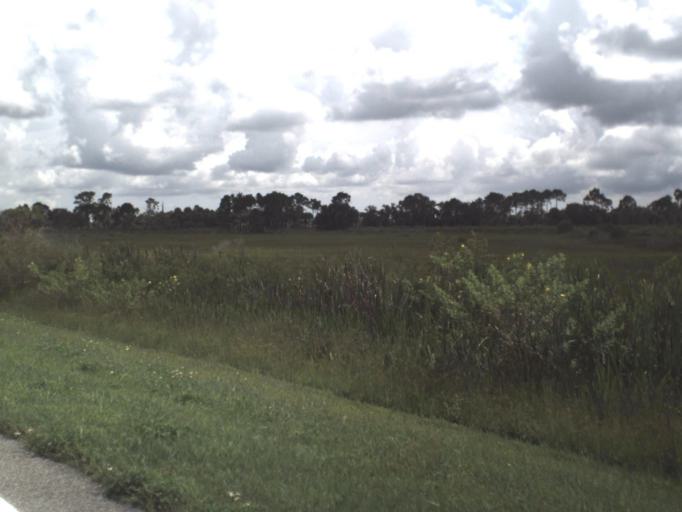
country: US
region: Florida
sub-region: Sarasota County
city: Warm Mineral Springs
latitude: 27.2105
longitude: -82.2573
